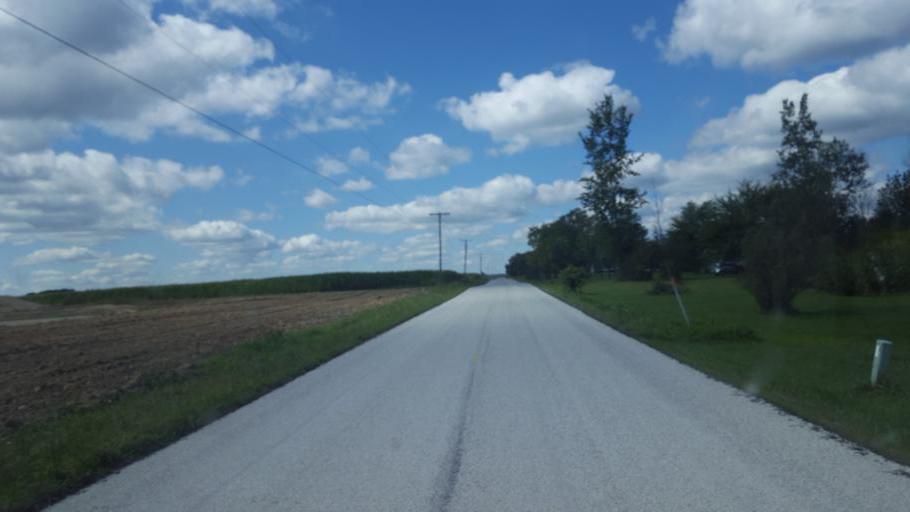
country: US
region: Ohio
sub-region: Wayne County
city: West Salem
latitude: 40.9740
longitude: -82.2158
